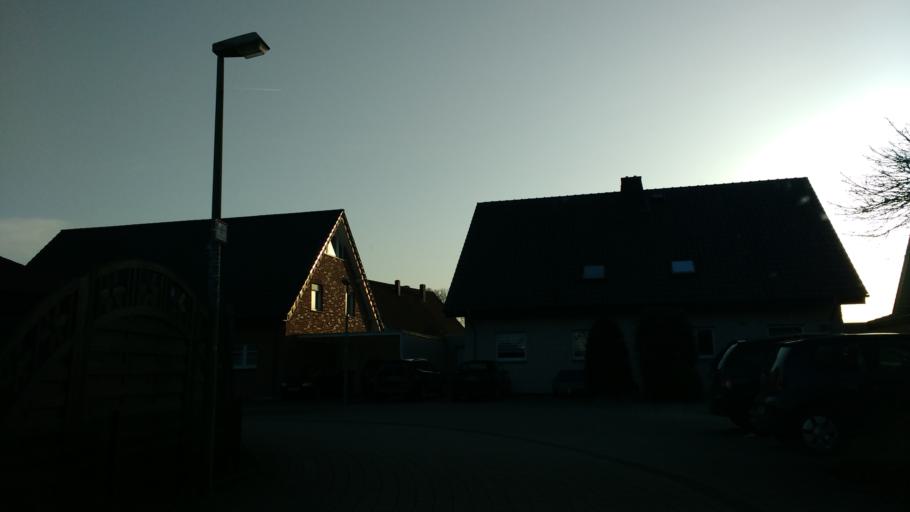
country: DE
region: North Rhine-Westphalia
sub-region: Regierungsbezirk Detmold
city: Hovelhof
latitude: 51.7816
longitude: 8.7106
